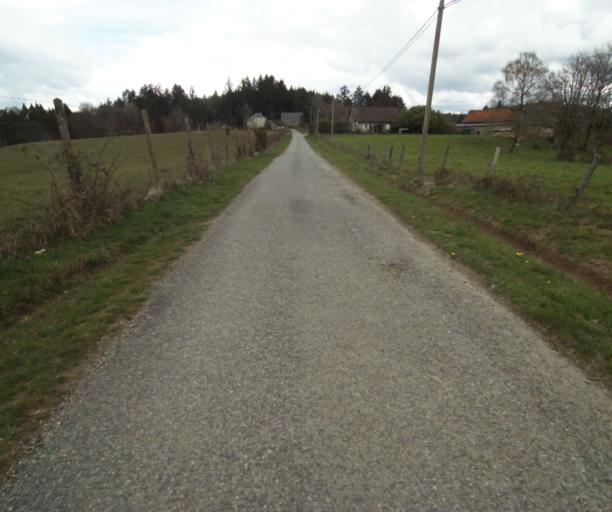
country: FR
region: Limousin
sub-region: Departement de la Correze
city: Correze
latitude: 45.2871
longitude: 1.9303
